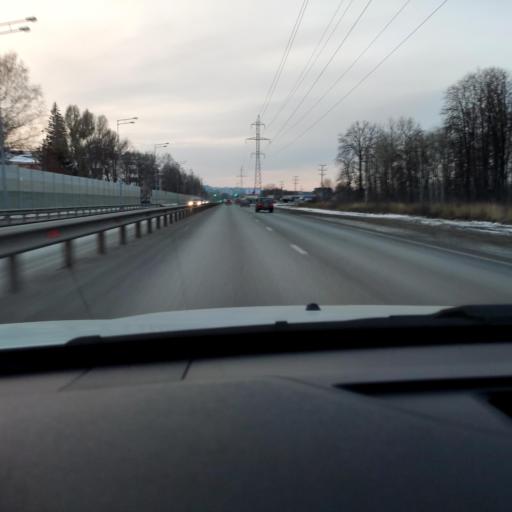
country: RU
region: Samara
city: Novosemeykino
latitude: 53.3493
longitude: 50.2301
